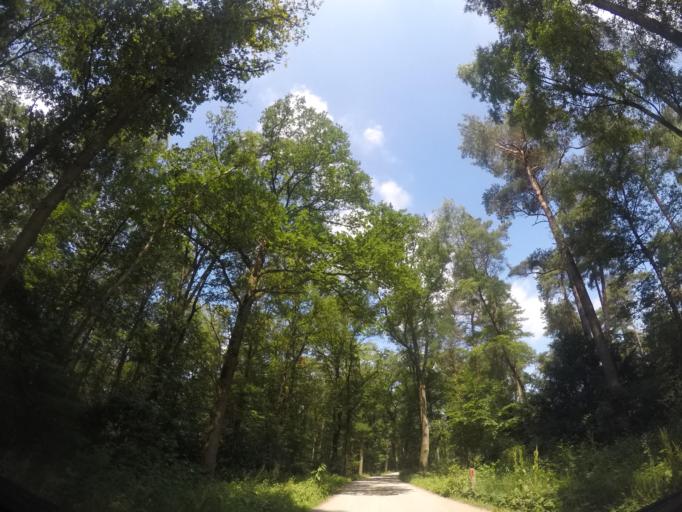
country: NL
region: Overijssel
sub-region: Gemeente Dalfsen
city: Dalfsen
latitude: 52.4805
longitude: 6.2610
